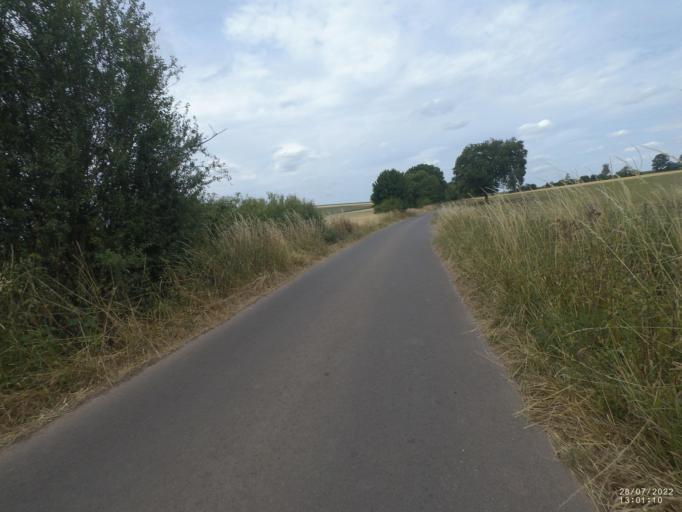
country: DE
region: Rheinland-Pfalz
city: Kalenborn-Scheuern
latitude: 50.2659
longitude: 6.6100
